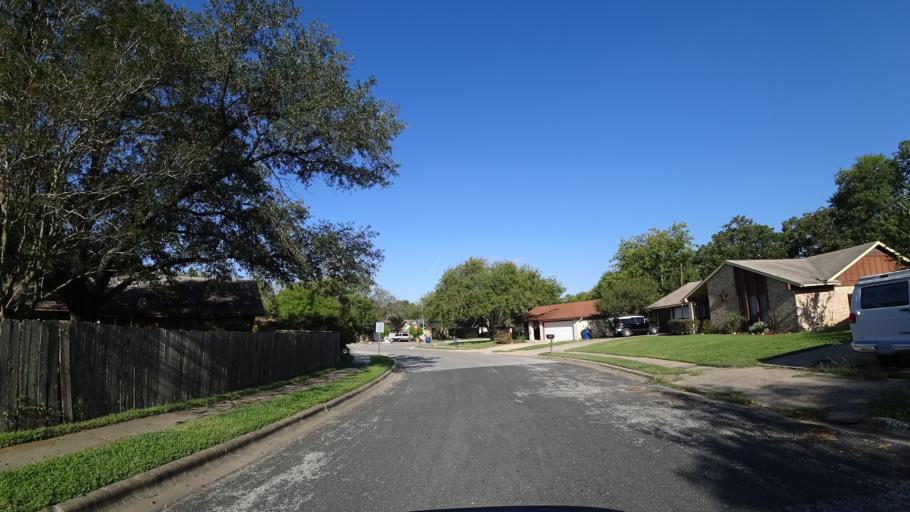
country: US
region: Texas
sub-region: Travis County
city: Rollingwood
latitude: 30.2126
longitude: -97.8127
